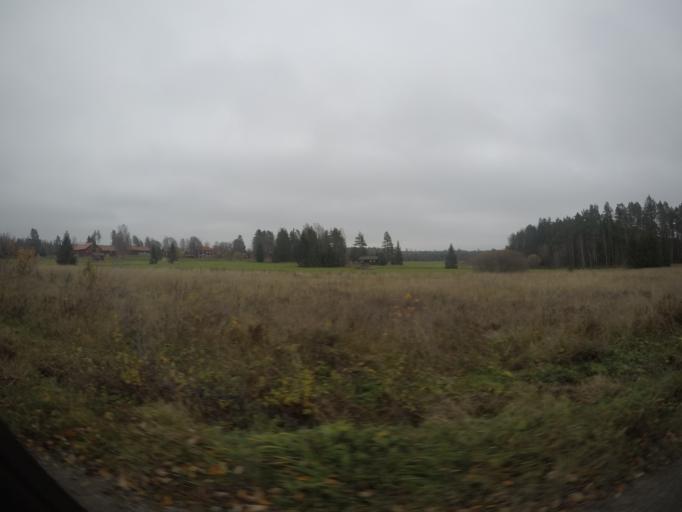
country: SE
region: Vaestmanland
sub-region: Surahammars Kommun
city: Ramnas
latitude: 59.7283
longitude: 16.0992
